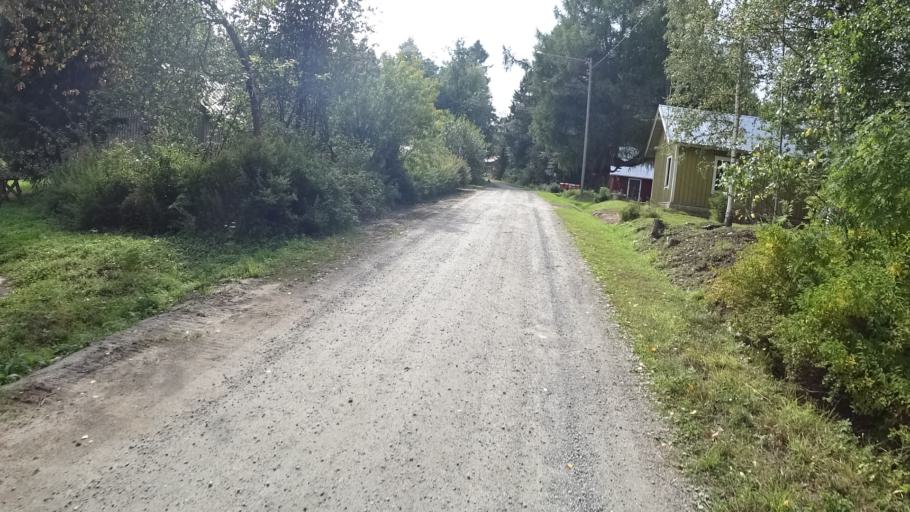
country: FI
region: North Karelia
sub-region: Joensuu
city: Ilomantsi
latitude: 62.6374
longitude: 31.2813
